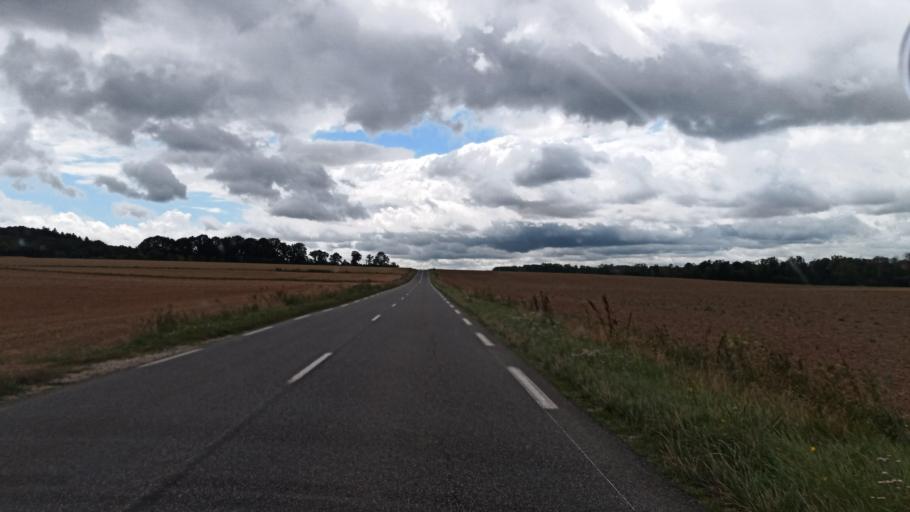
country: FR
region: Ile-de-France
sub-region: Departement de Seine-et-Marne
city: Voulx
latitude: 48.3178
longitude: 2.9502
